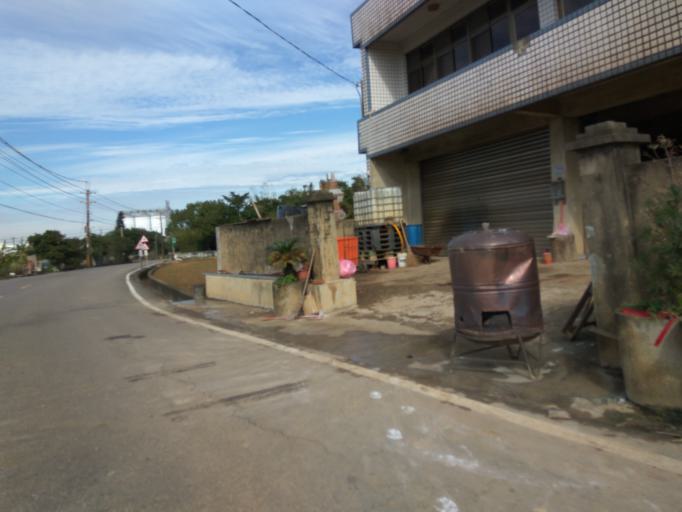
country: TW
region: Taiwan
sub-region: Hsinchu
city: Zhubei
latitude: 24.9931
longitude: 121.0961
